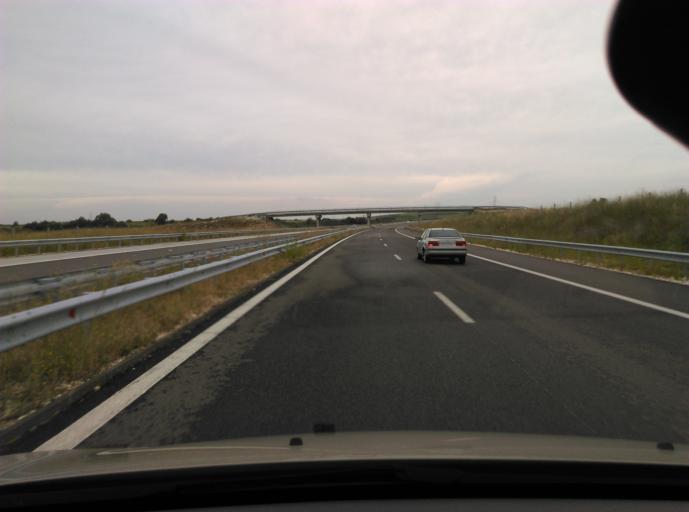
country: BG
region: Stara Zagora
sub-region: Obshtina Chirpan
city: Chirpan
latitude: 42.1205
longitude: 25.3807
